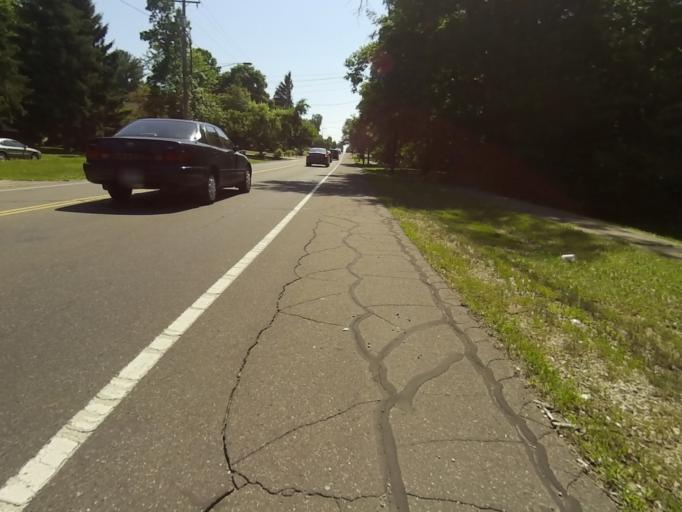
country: US
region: Ohio
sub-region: Summit County
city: Stow
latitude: 41.1667
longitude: -81.4351
